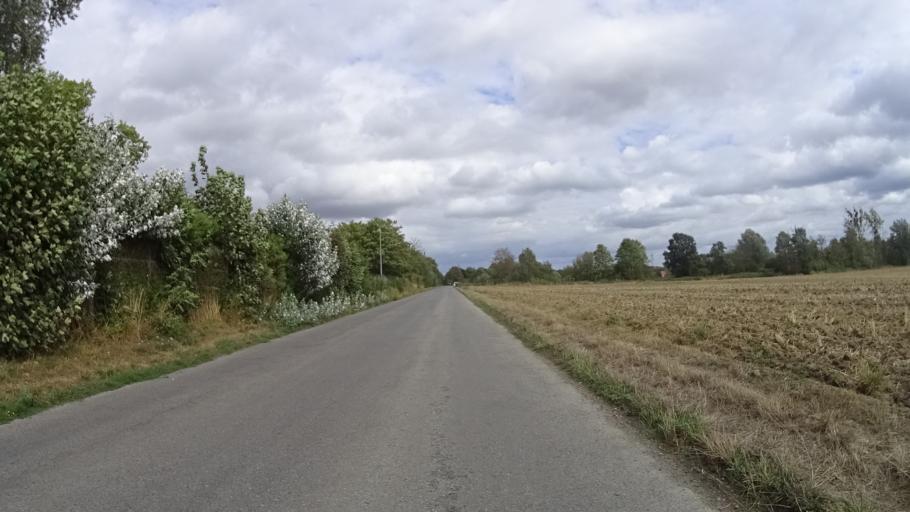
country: FR
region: Picardie
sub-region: Departement de l'Aisne
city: Beautor
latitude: 49.6490
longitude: 3.3317
